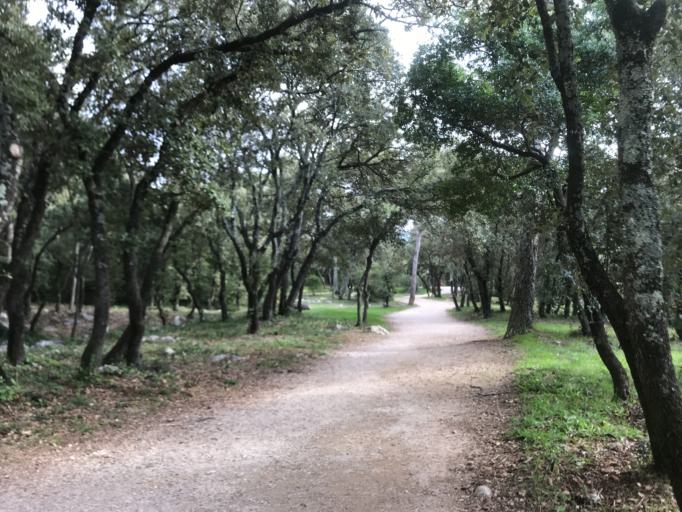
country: FR
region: Languedoc-Roussillon
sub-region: Departement de l'Herault
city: Clapiers
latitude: 43.6405
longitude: 3.8663
